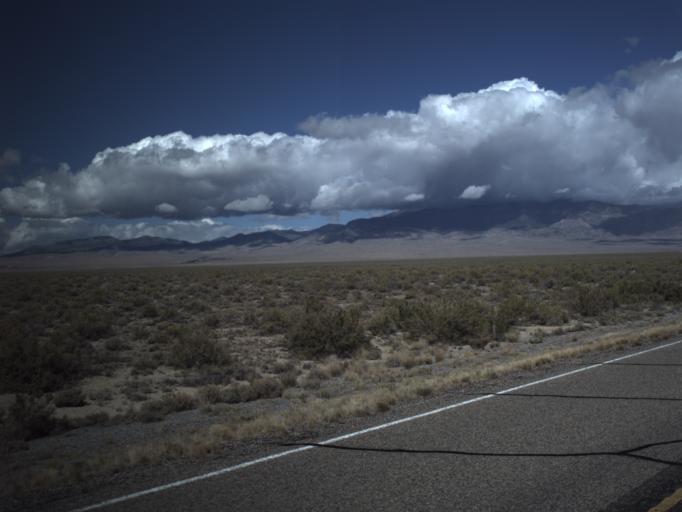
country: US
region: Nevada
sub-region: White Pine County
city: McGill
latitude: 39.0111
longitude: -114.0351
